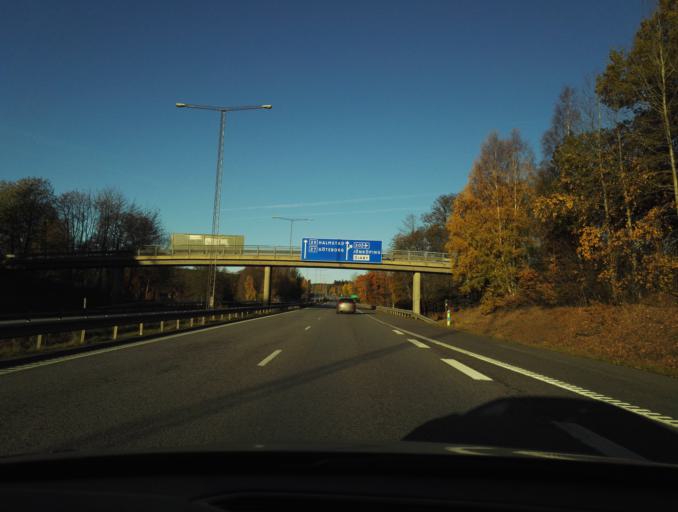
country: SE
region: Kronoberg
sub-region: Vaxjo Kommun
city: Vaexjoe
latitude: 56.8927
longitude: 14.7467
